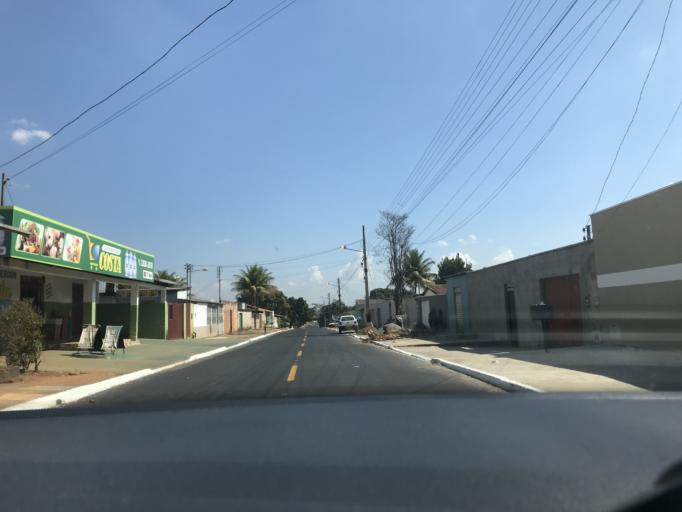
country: BR
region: Goias
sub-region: Senador Canedo
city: Senador Canedo
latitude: -16.6514
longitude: -49.1592
